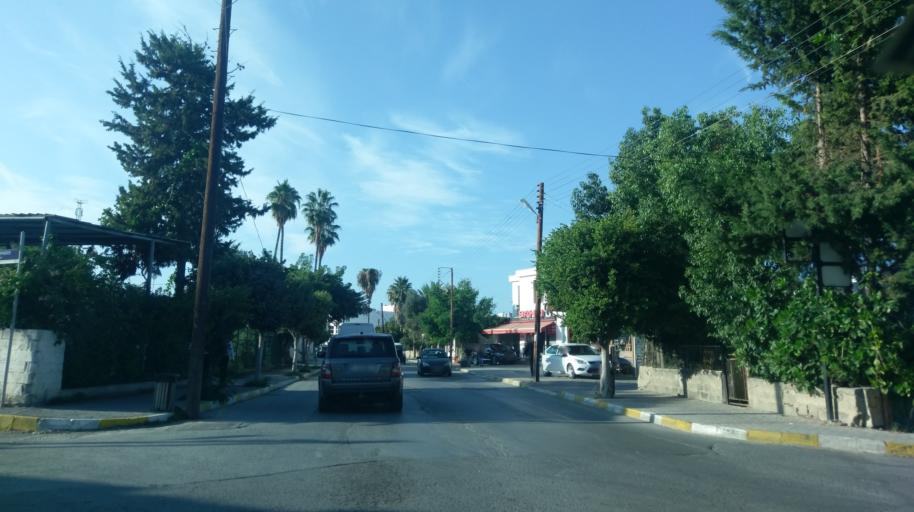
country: CY
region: Keryneia
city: Kyrenia
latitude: 35.3379
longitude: 33.3245
